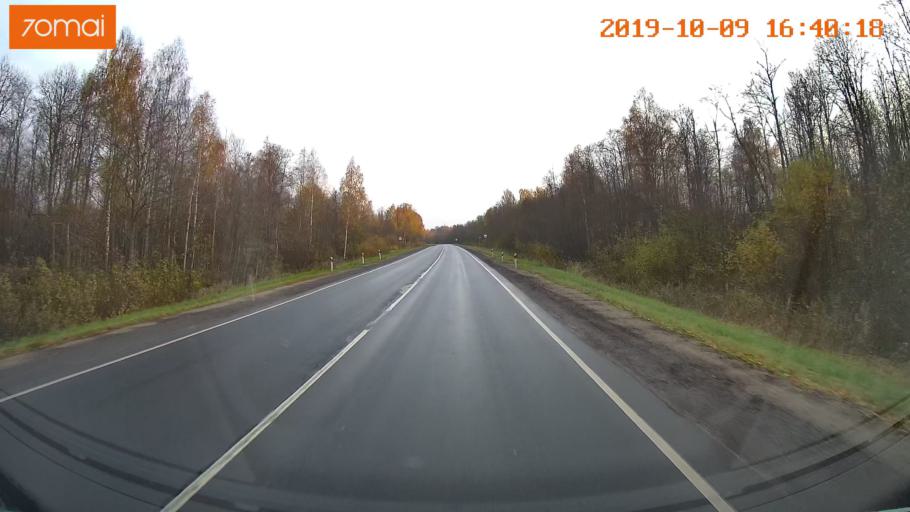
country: RU
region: Kostroma
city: Volgorechensk
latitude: 57.4854
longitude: 41.0590
